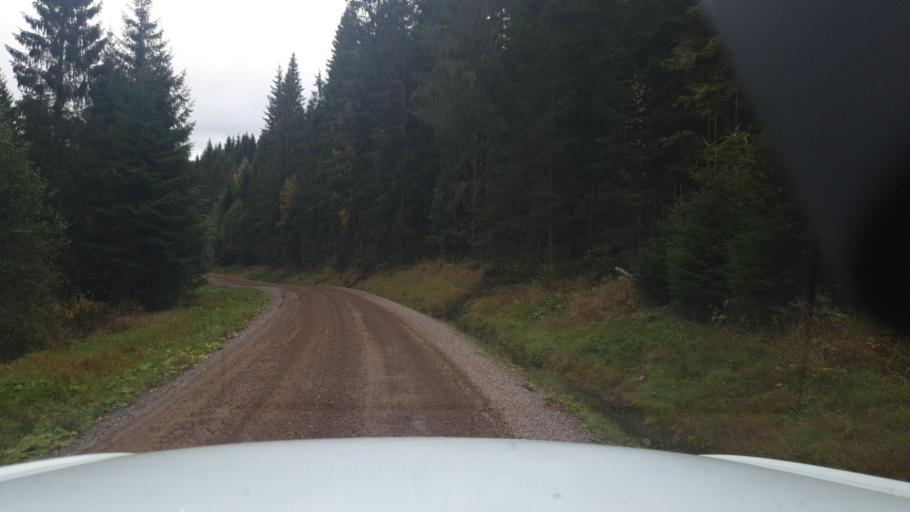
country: SE
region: Vaermland
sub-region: Eda Kommun
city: Charlottenberg
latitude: 60.0436
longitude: 12.5753
